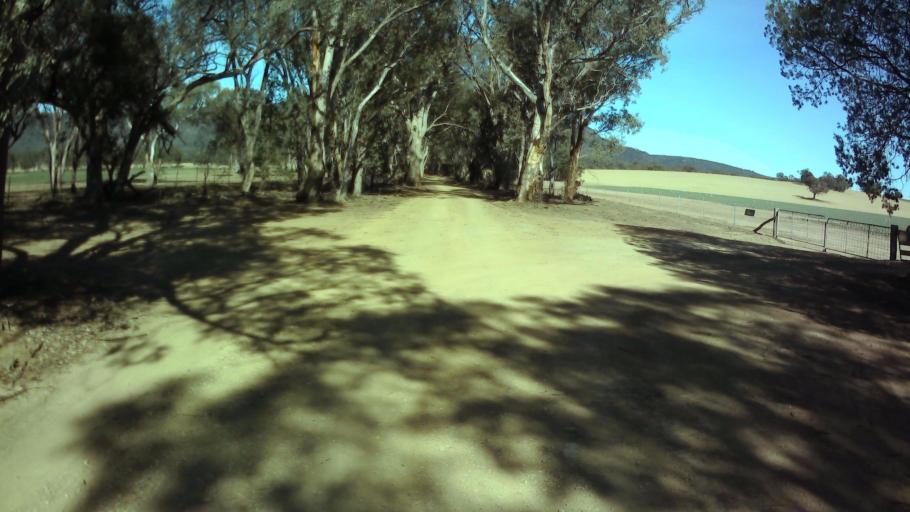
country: AU
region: New South Wales
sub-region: Weddin
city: Grenfell
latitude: -33.9013
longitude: 148.0282
